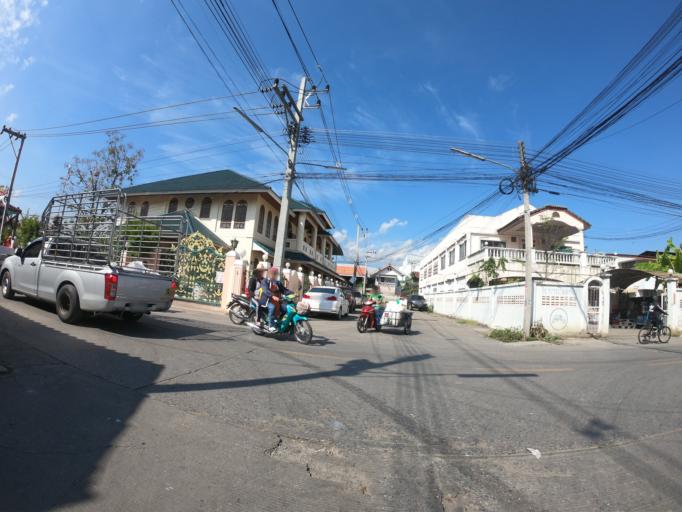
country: TH
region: Chiang Mai
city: Chiang Mai
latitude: 18.7982
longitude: 98.9966
